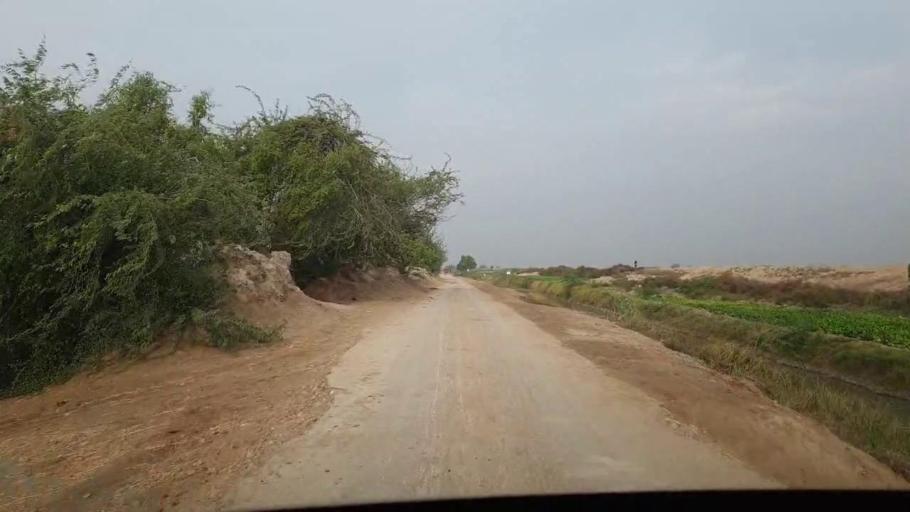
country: PK
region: Sindh
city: Chuhar Jamali
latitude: 24.3981
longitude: 67.9701
